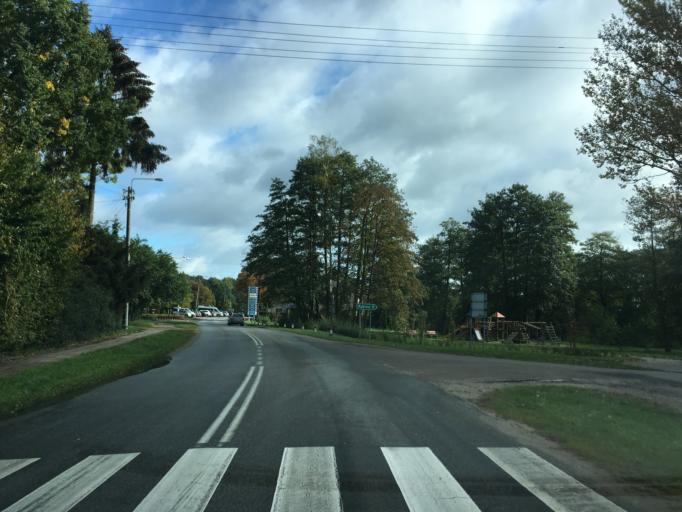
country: PL
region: Pomeranian Voivodeship
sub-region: Powiat nowodworski
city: Stegna
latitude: 54.3318
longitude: 19.0319
